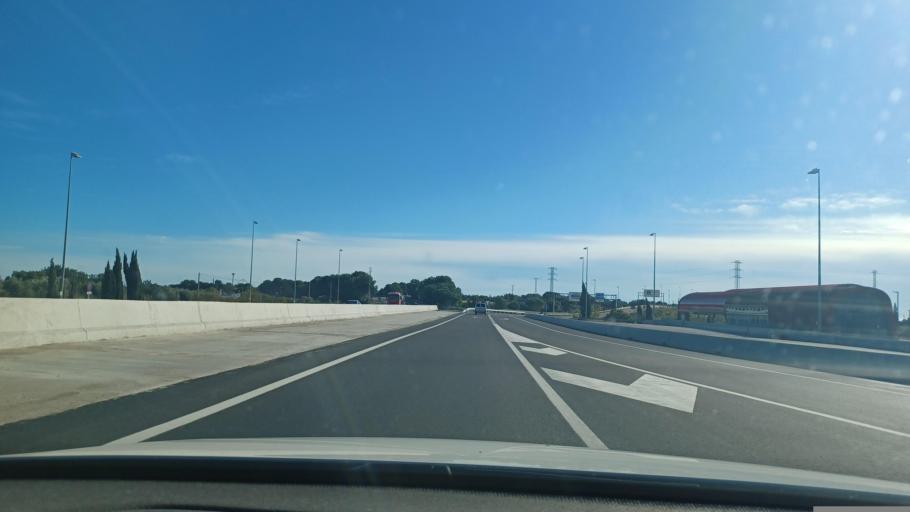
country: ES
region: Catalonia
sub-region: Provincia de Tarragona
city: Vila-seca
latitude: 41.1085
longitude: 1.1304
